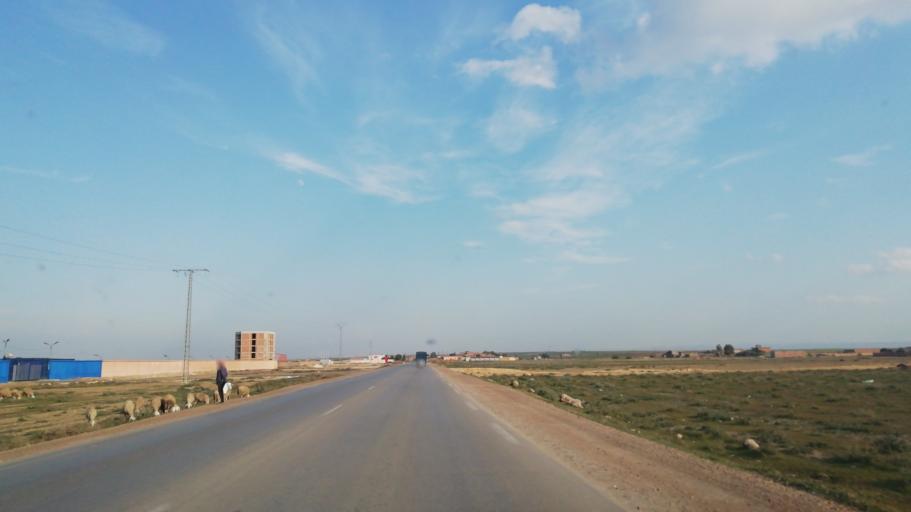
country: DZ
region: Relizane
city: Relizane
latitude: 35.8979
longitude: 0.5795
